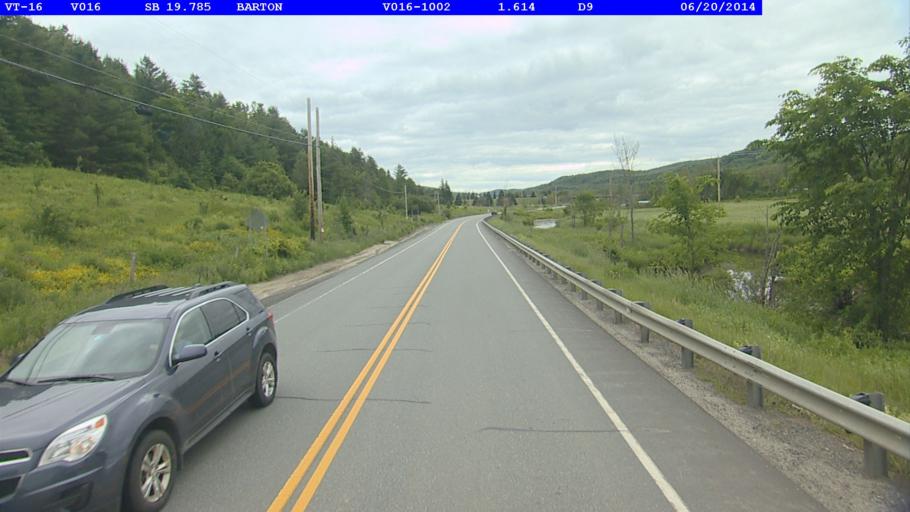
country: US
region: Vermont
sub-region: Orleans County
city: Newport
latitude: 44.7403
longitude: -72.1814
